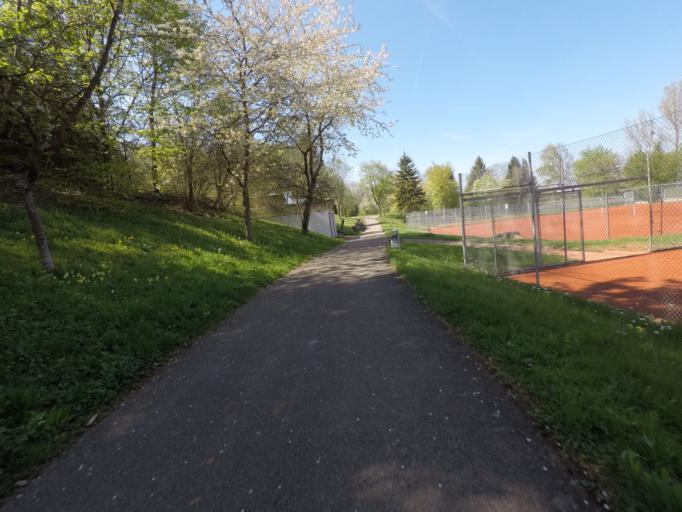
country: DE
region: Baden-Wuerttemberg
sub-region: Tuebingen Region
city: Pfullingen
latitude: 48.4501
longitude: 9.2298
